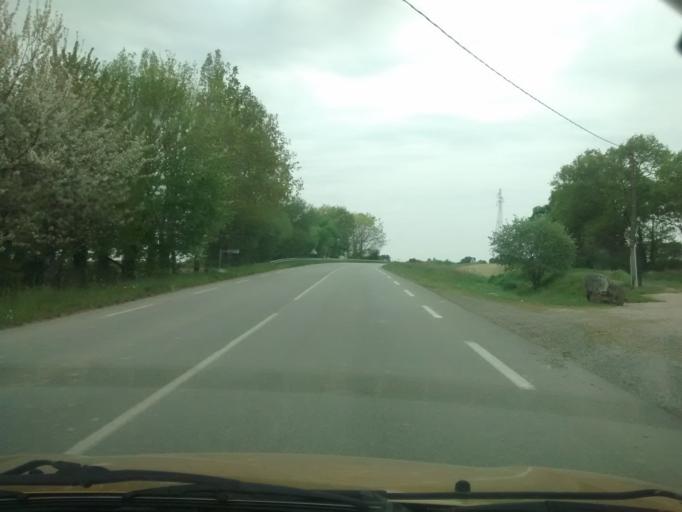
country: FR
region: Brittany
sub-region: Departement du Morbihan
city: Ambon
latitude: 47.5933
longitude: -2.5489
